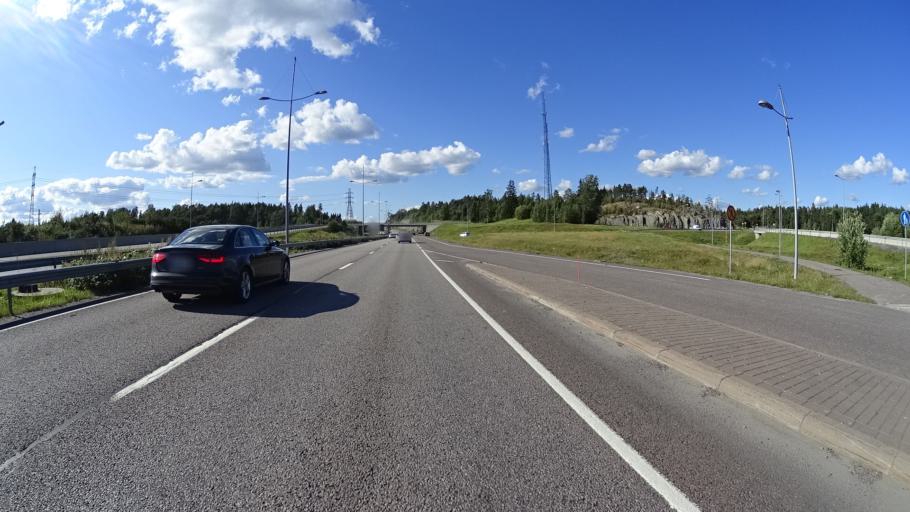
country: FI
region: Uusimaa
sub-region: Helsinki
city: Vantaa
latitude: 60.2433
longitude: 25.1498
